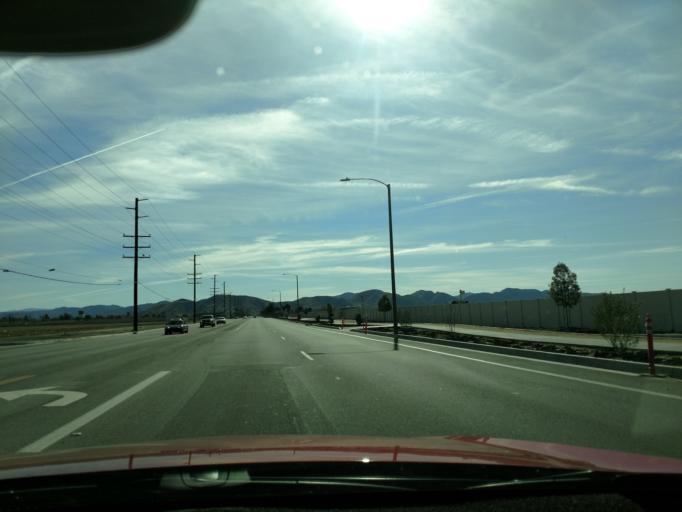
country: US
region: California
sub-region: Riverside County
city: Hemet
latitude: 33.7420
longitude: -117.0067
